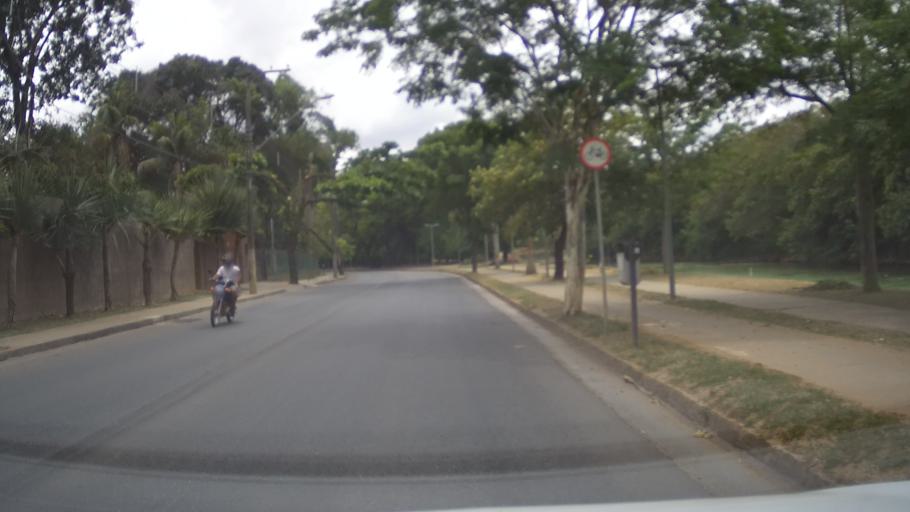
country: BR
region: Minas Gerais
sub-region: Belo Horizonte
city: Belo Horizonte
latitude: -19.8551
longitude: -43.9983
